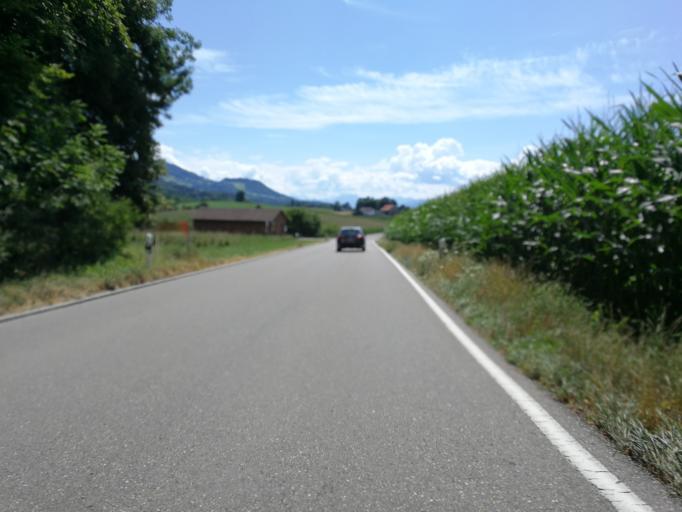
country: CH
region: Zurich
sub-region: Bezirk Hinwil
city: Wetzikon / Kempten
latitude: 47.3189
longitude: 8.8169
